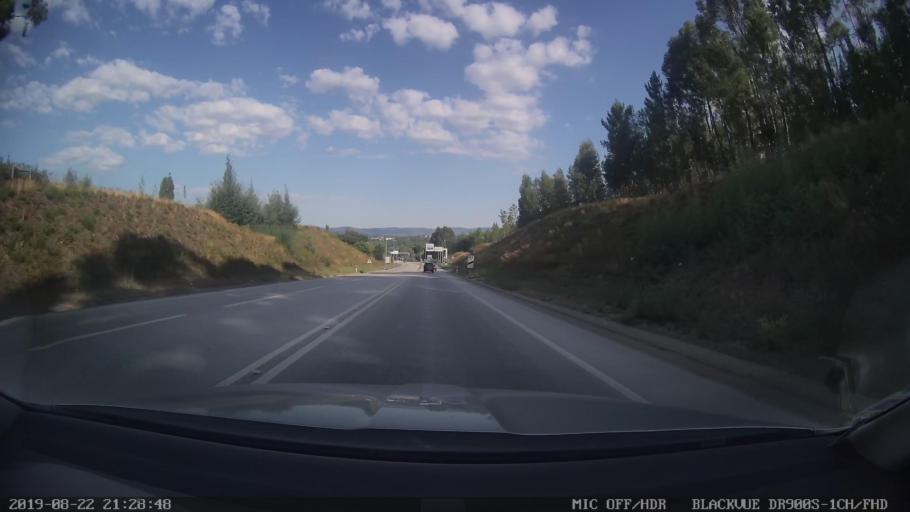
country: PT
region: Leiria
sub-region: Pedrogao Grande
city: Pedrogao Grande
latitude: 39.8969
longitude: -8.1251
